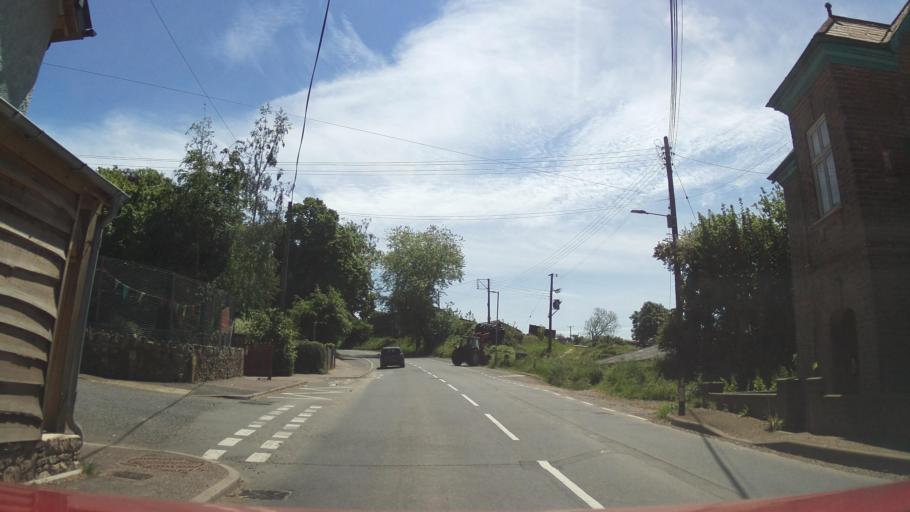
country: GB
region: England
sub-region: Devon
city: Honiton
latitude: 50.8091
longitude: -3.2317
